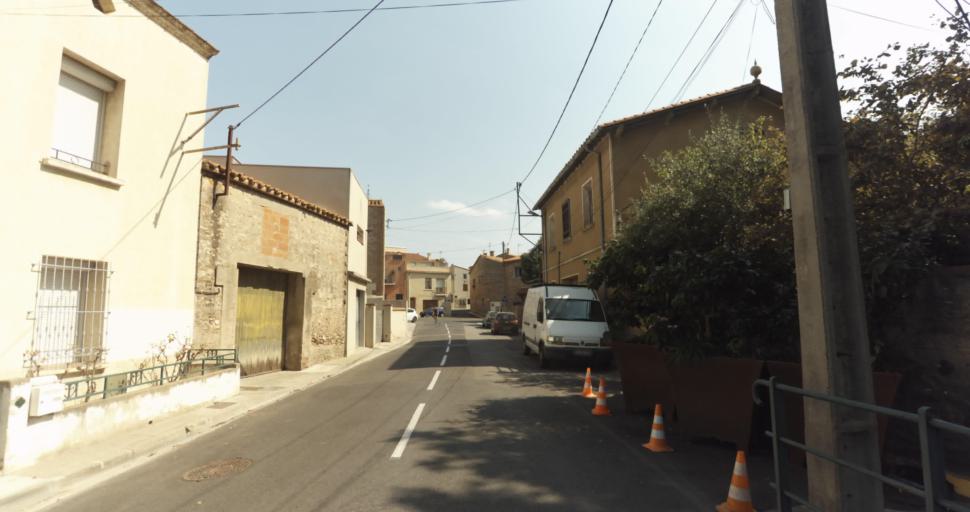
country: FR
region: Languedoc-Roussillon
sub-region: Departement des Pyrenees-Orientales
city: Latour-Bas-Elne
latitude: 42.6047
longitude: 3.0012
